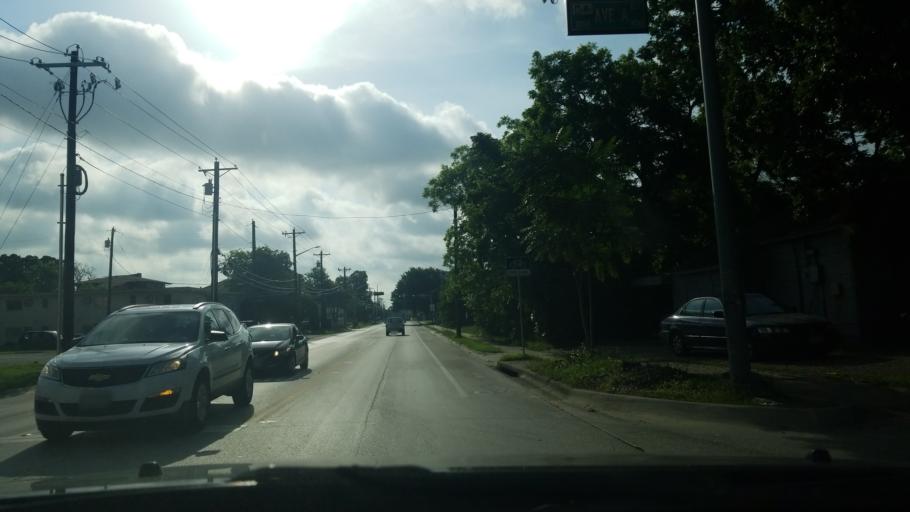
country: US
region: Texas
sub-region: Denton County
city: Denton
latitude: 33.2067
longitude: -97.1460
